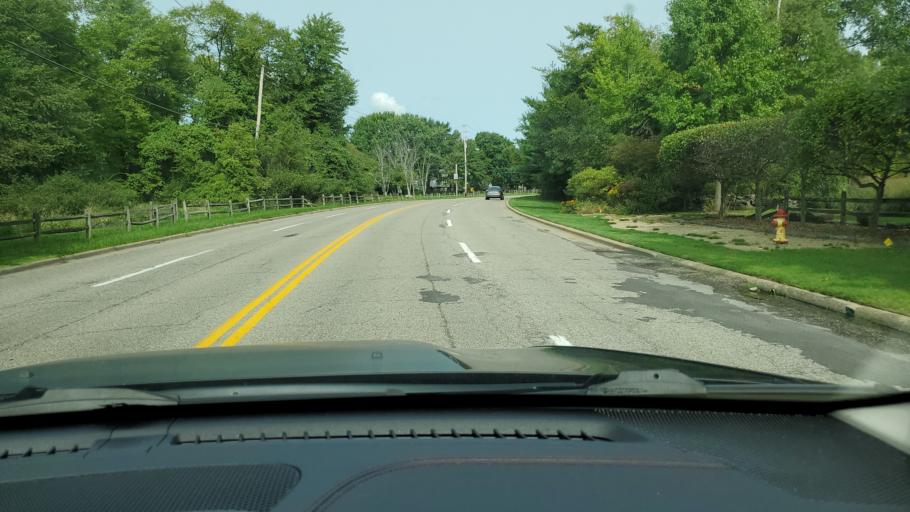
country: US
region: Ohio
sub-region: Mahoning County
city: Boardman
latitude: 40.9918
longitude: -80.6717
